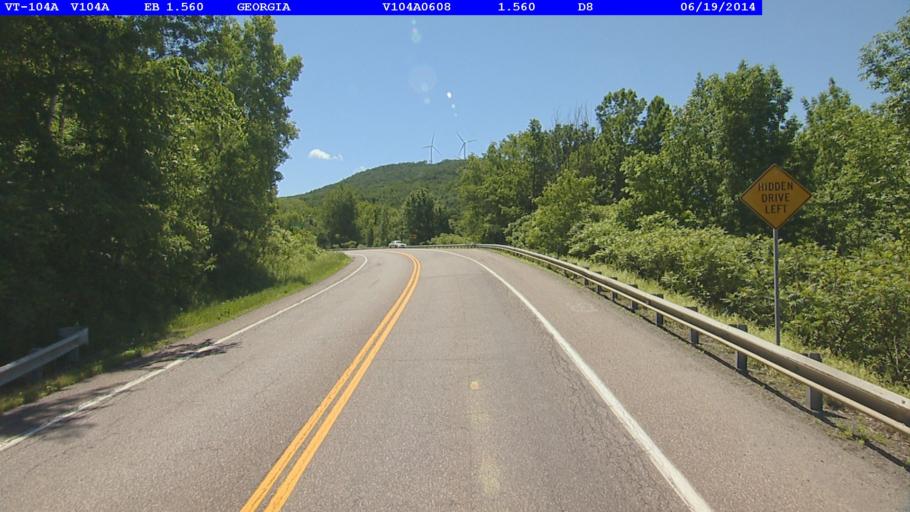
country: US
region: Vermont
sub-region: Chittenden County
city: Milton
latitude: 44.6812
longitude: -73.0849
